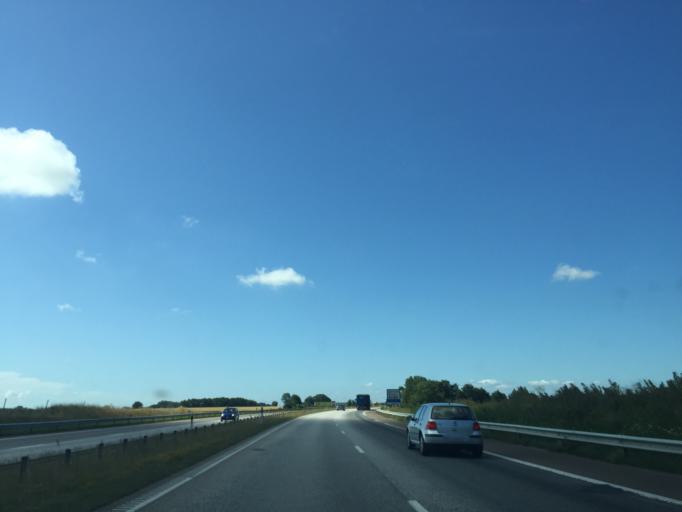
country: SE
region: Skane
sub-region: Angelholms Kommun
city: AEngelholm
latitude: 56.2115
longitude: 12.8844
